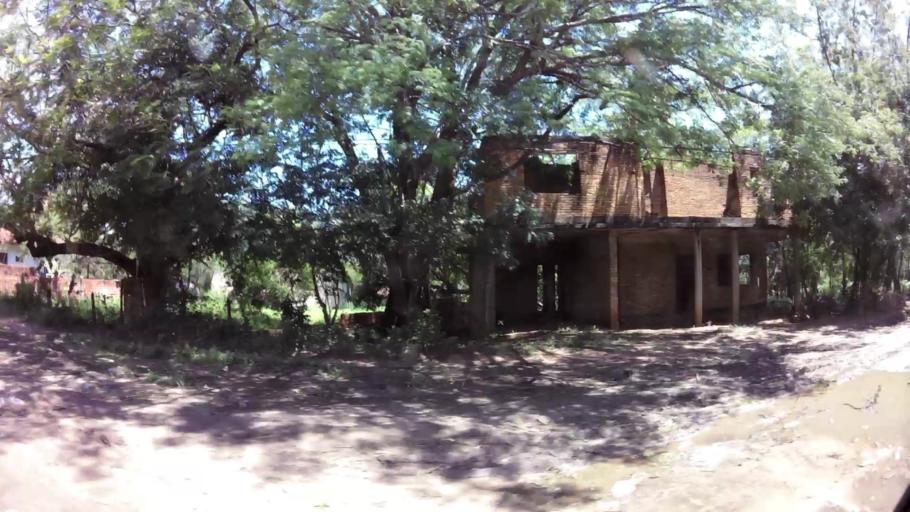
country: PY
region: Central
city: Colonia Mariano Roque Alonso
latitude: -25.1961
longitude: -57.5476
